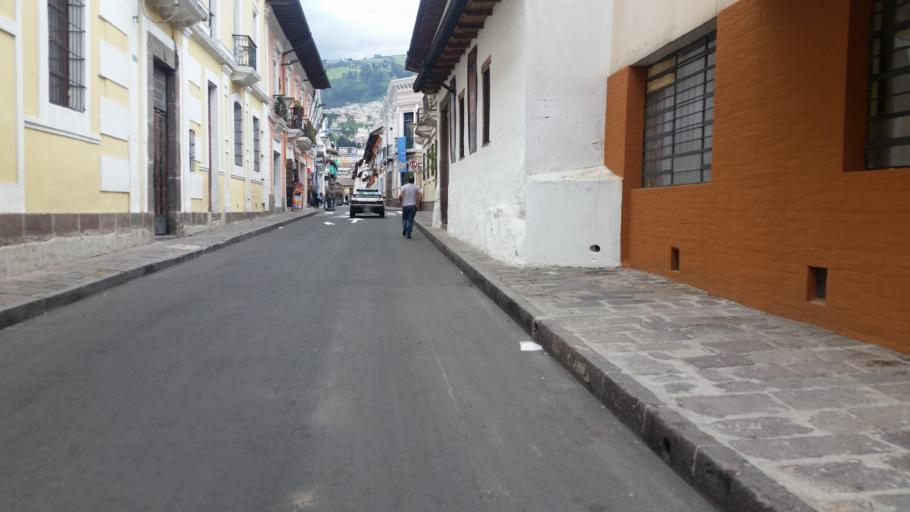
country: EC
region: Pichincha
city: Quito
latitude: -0.2238
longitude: -78.5091
